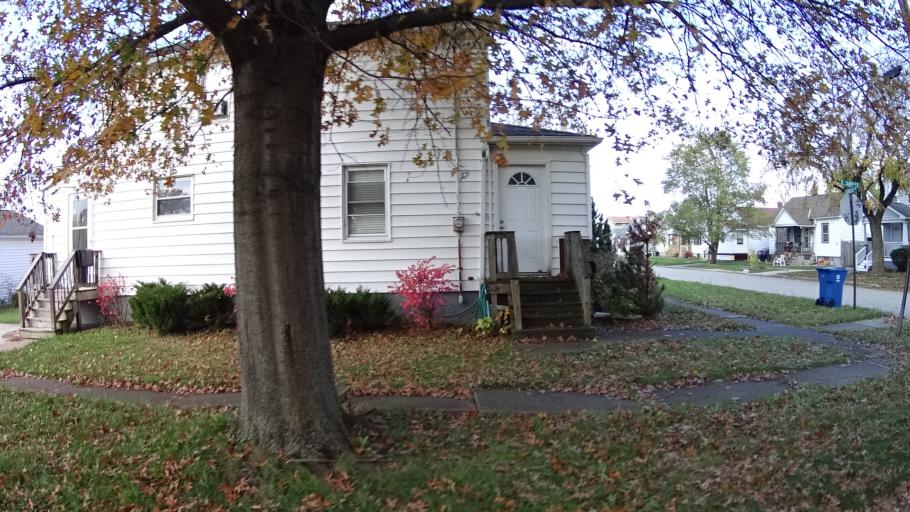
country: US
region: Ohio
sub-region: Lorain County
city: Sheffield
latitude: 41.4401
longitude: -82.1095
